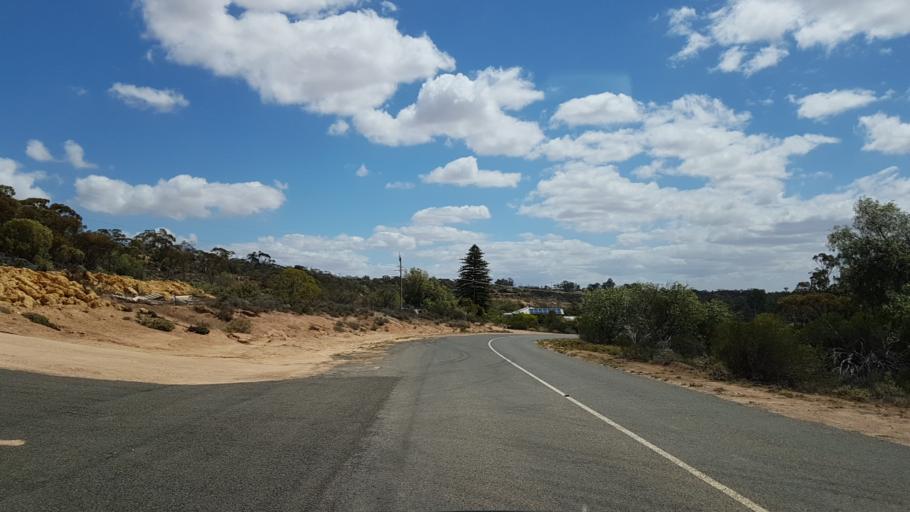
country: AU
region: South Australia
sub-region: Loxton Waikerie
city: Waikerie
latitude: -34.1845
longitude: 140.0169
